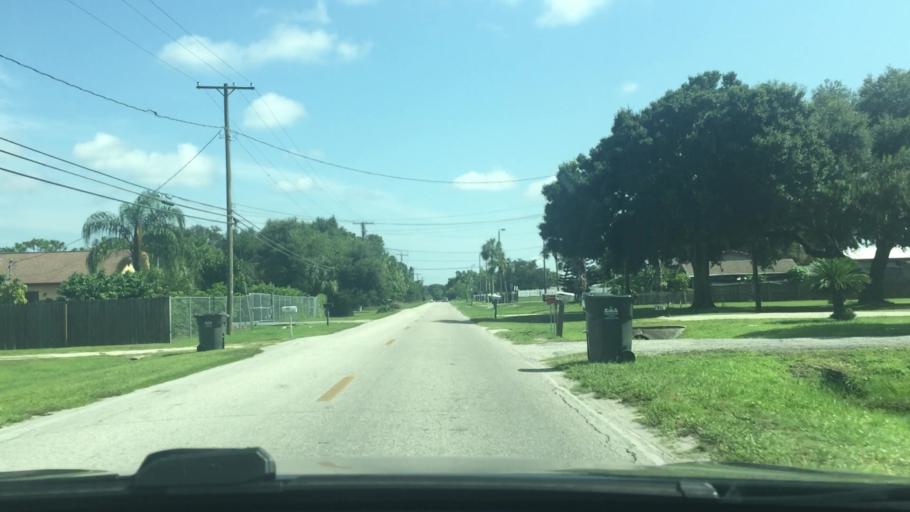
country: US
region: Florida
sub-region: Hillsborough County
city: Ruskin
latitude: 27.6976
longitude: -82.4437
